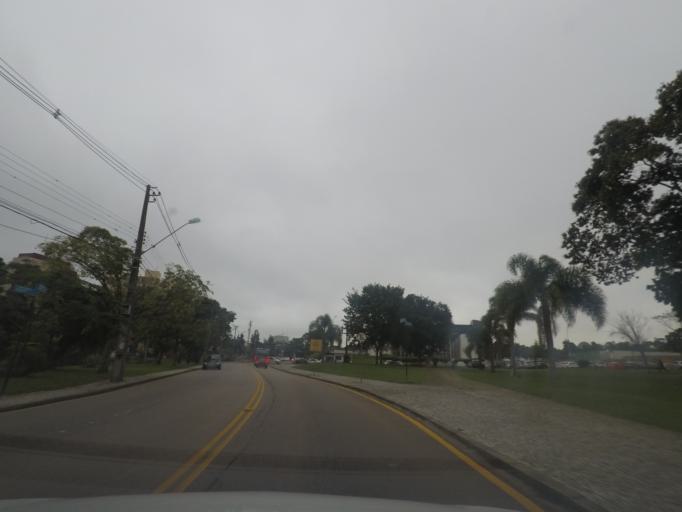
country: BR
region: Parana
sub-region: Curitiba
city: Curitiba
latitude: -25.4143
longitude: -49.2699
